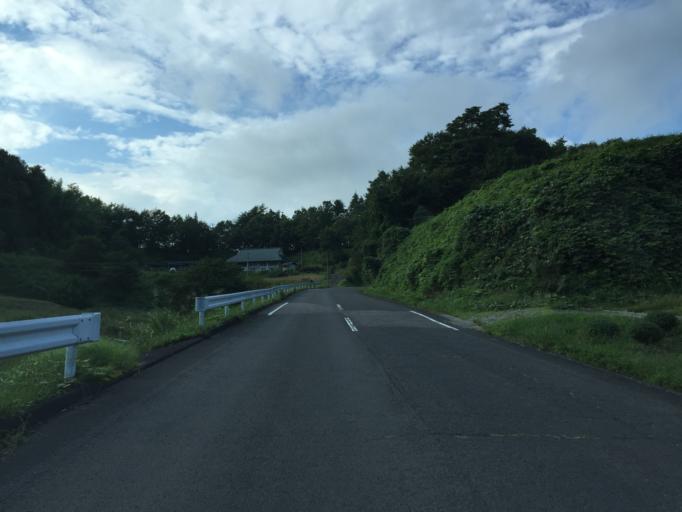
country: JP
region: Fukushima
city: Fukushima-shi
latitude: 37.6525
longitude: 140.5762
